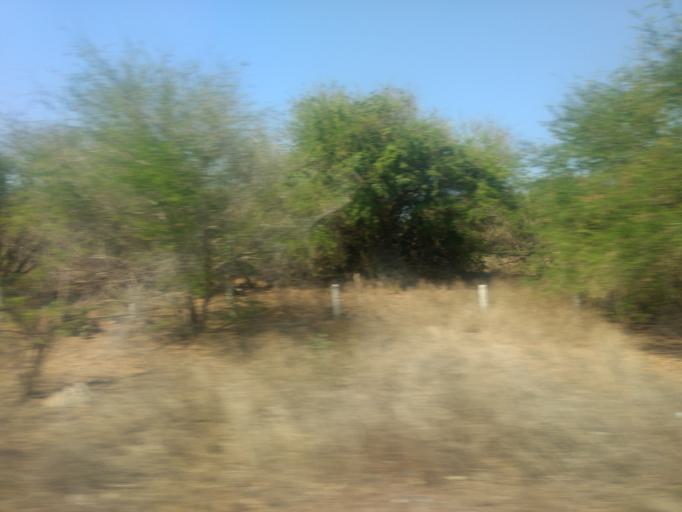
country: MX
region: Colima
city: El Colomo
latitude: 18.9598
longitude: -104.1466
